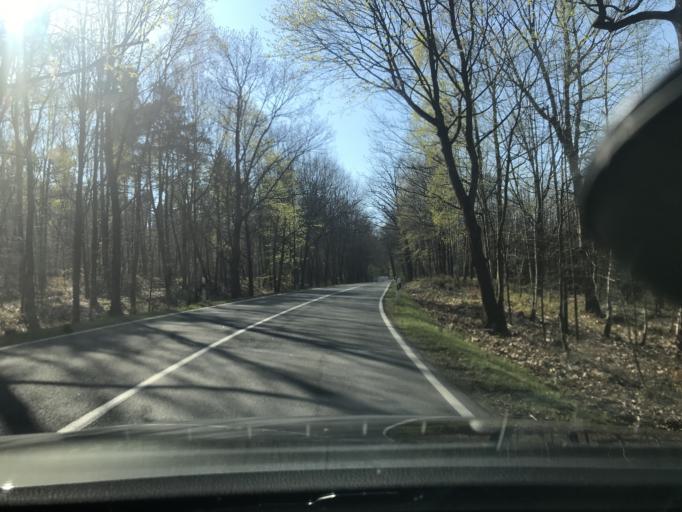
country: DE
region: Saxony-Anhalt
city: Bad Schmiedeberg
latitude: 51.6720
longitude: 12.6948
